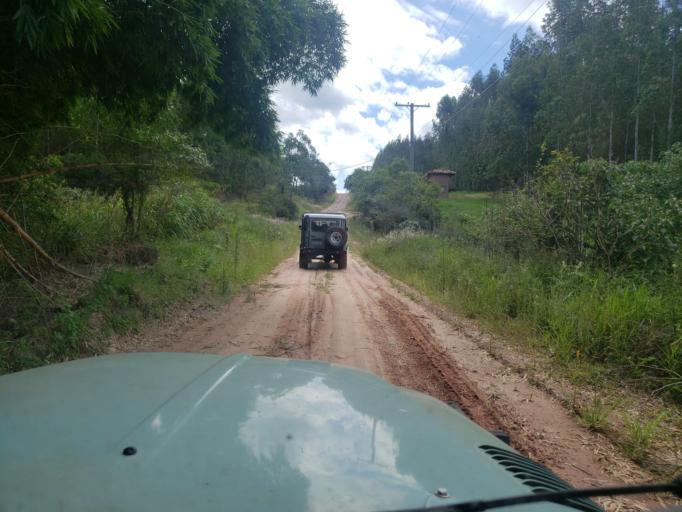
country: BR
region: Sao Paulo
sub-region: Conchal
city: Conchal
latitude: -22.2493
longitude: -47.0855
